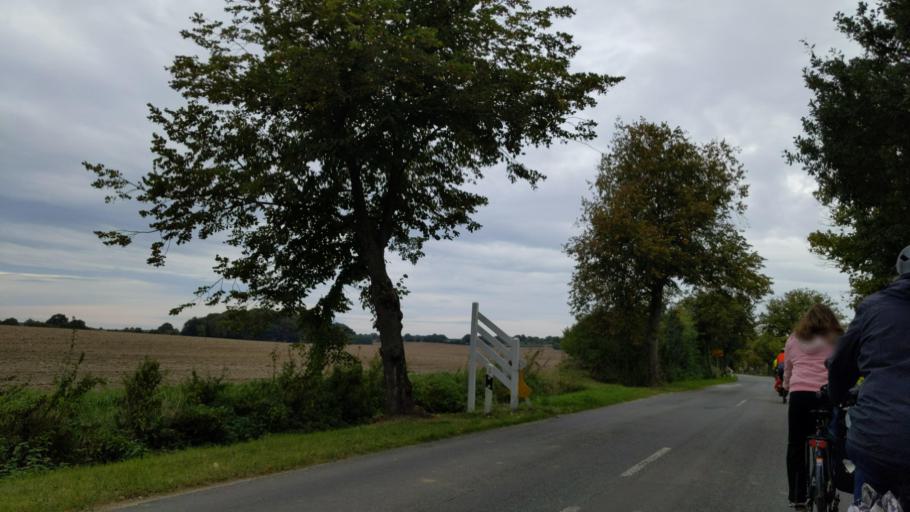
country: DE
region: Mecklenburg-Vorpommern
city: Schlagsdorf
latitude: 53.7619
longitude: 10.8182
